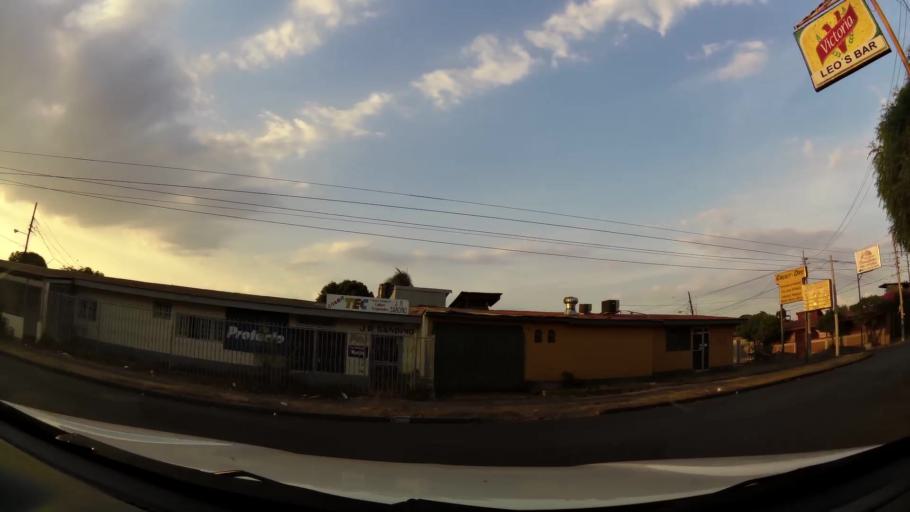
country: NI
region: Managua
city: Managua
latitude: 12.1424
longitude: -86.2546
